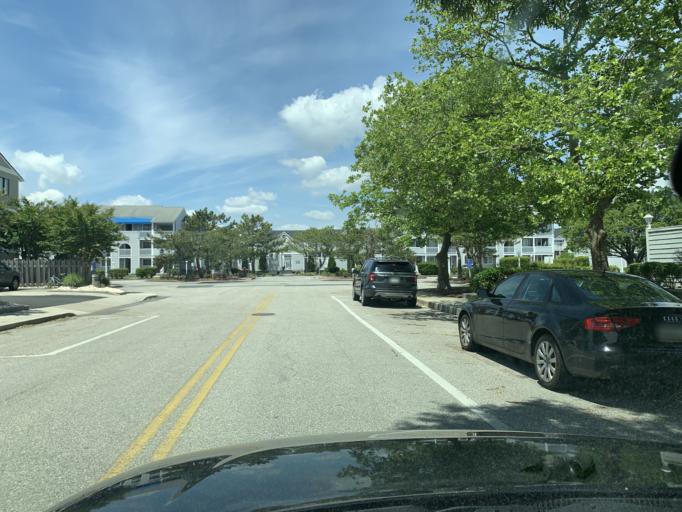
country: US
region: Maryland
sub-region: Worcester County
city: Ocean City
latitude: 38.4288
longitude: -75.0596
